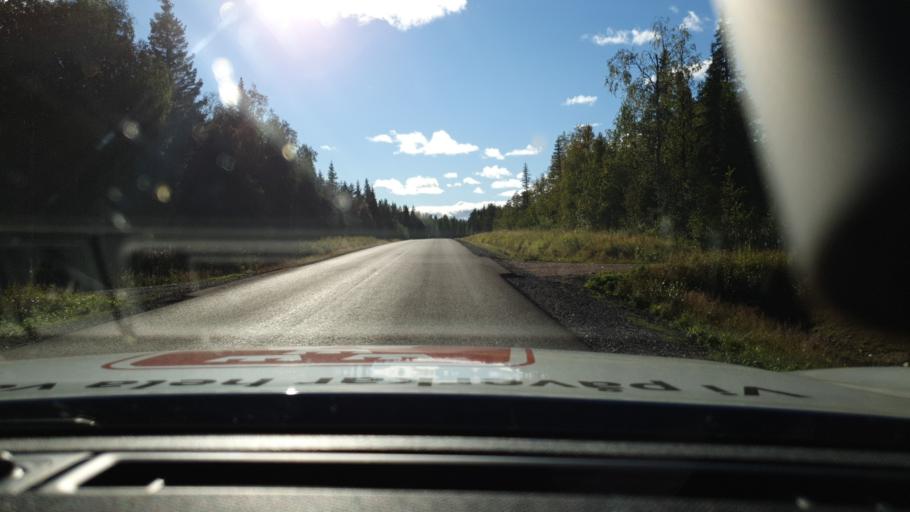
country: SE
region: Norrbotten
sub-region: Overkalix Kommun
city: OEverkalix
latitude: 67.0668
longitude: 22.4192
